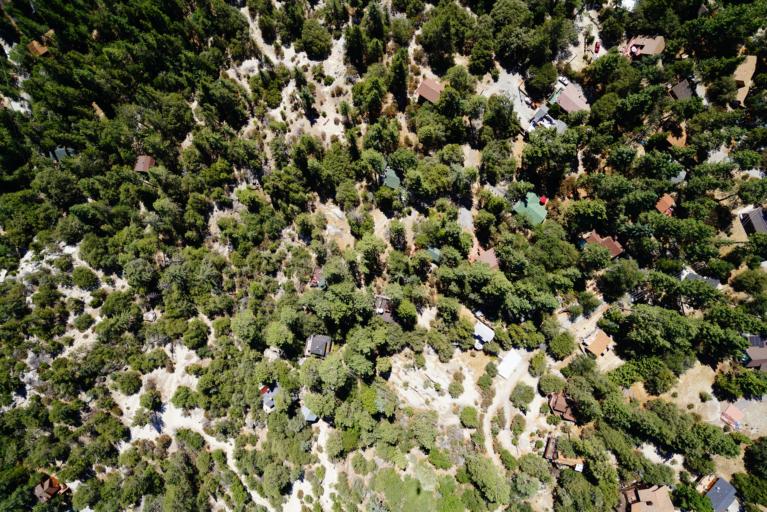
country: US
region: California
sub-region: Riverside County
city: Idyllwild-Pine Cove
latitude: 33.7600
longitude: -116.7356
